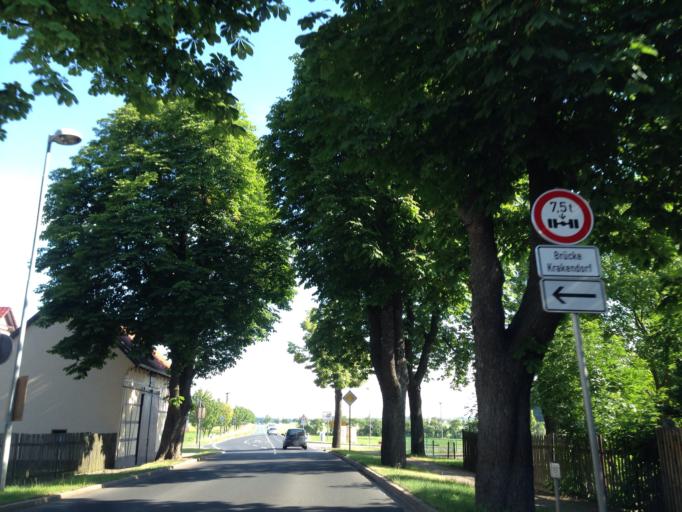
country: DE
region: Thuringia
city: Blankenhain
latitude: 50.8294
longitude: 11.3431
